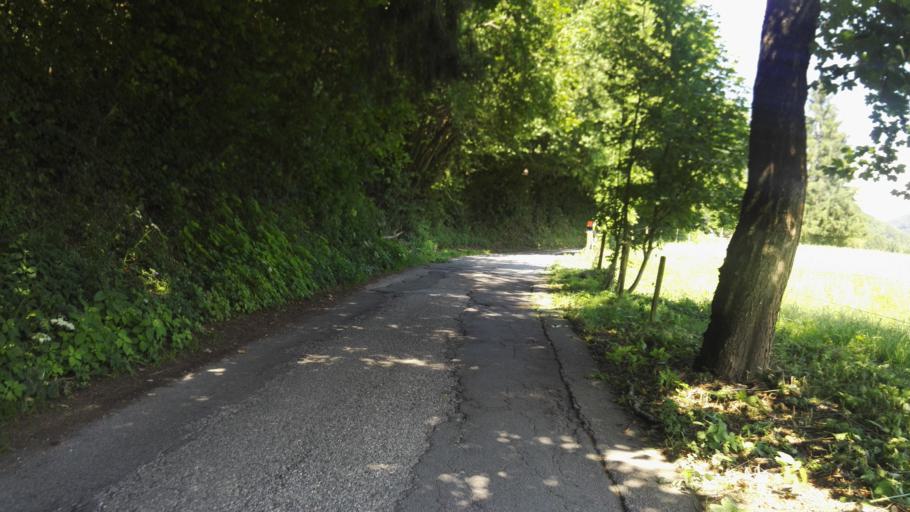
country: AT
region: Styria
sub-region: Politischer Bezirk Graz-Umgebung
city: Frohnleiten
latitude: 47.2332
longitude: 15.3126
